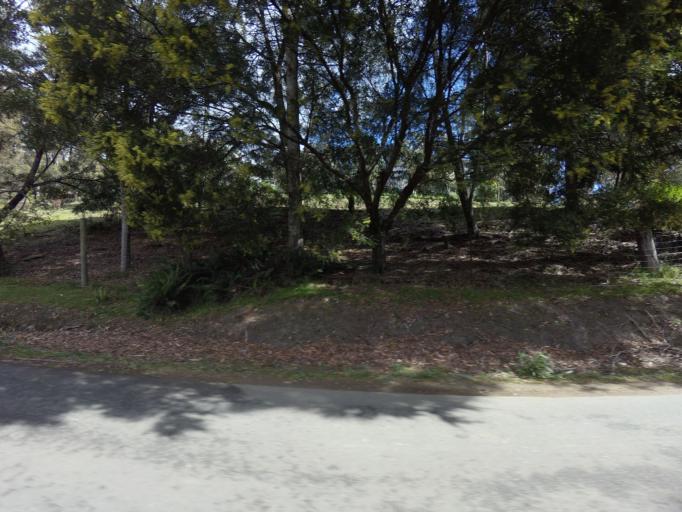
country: AU
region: Tasmania
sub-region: Huon Valley
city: Geeveston
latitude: -43.4164
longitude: 146.9647
